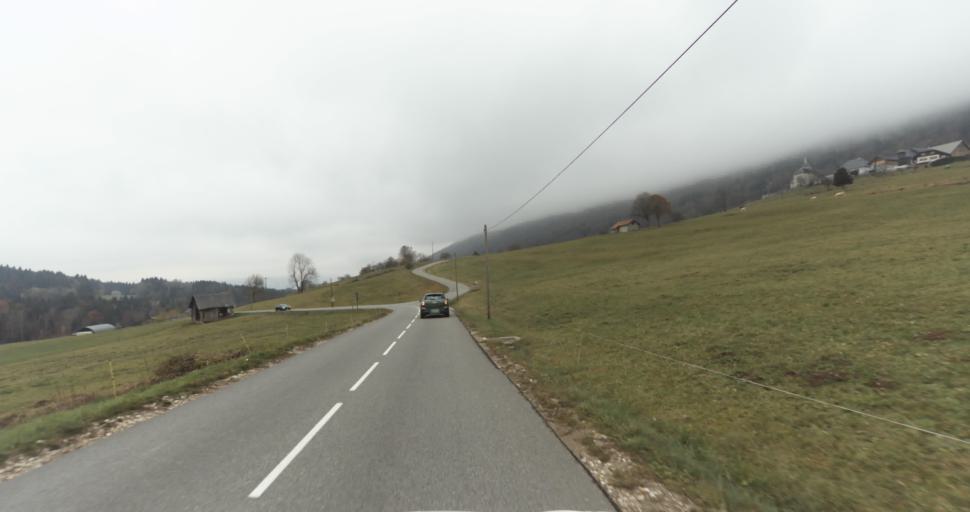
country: FR
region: Rhone-Alpes
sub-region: Departement de la Haute-Savoie
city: Saint-Jorioz
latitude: 45.7694
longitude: 6.1276
